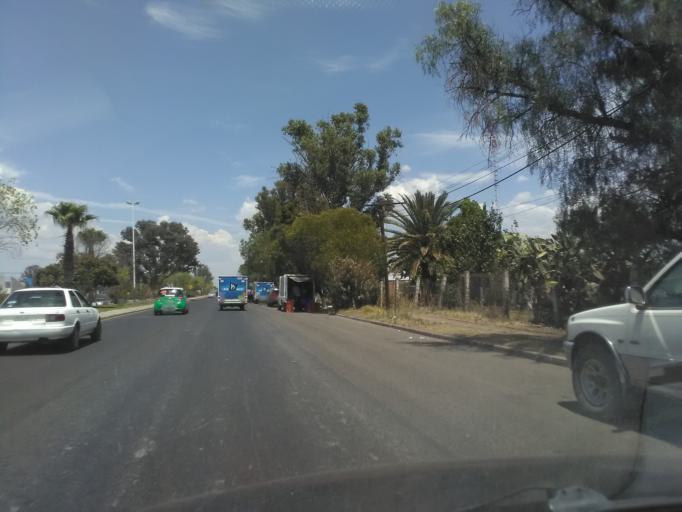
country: MX
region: Durango
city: Victoria de Durango
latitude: 24.0309
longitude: -104.6181
